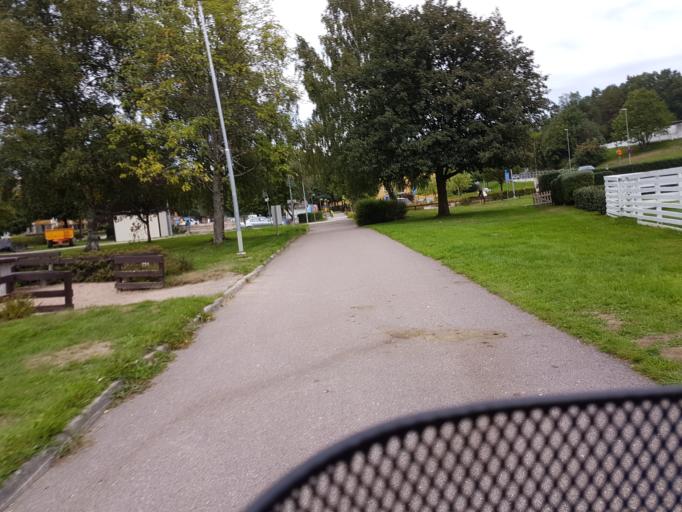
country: SE
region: Vaestra Goetaland
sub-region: Ale Kommun
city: Nodinge-Nol
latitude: 57.9125
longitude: 12.0684
